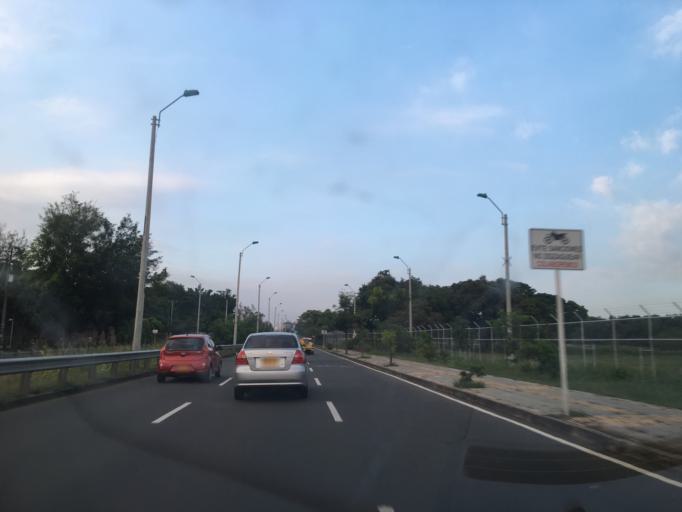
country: CO
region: Valle del Cauca
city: Cali
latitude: 3.3775
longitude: -76.5291
